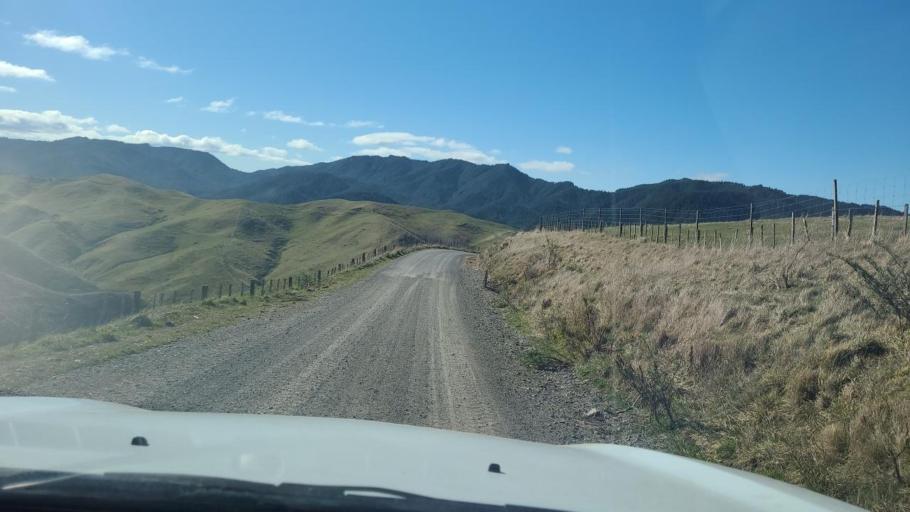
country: NZ
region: Hawke's Bay
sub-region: Napier City
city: Taradale
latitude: -39.1875
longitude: 176.4991
